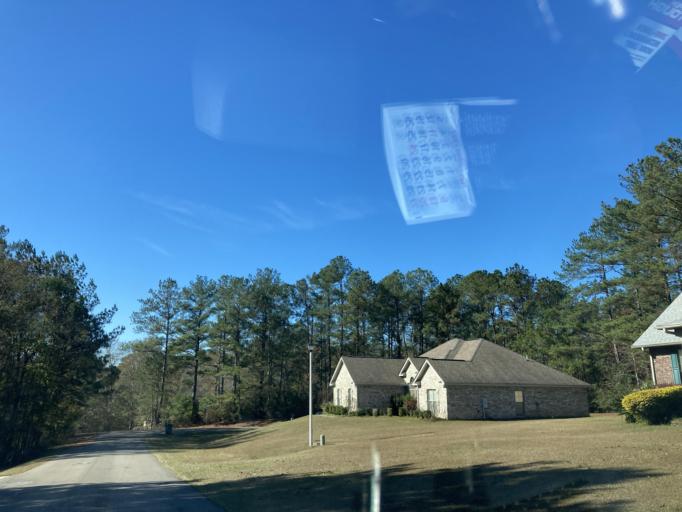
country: US
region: Mississippi
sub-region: Forrest County
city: Petal
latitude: 31.3354
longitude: -89.1688
